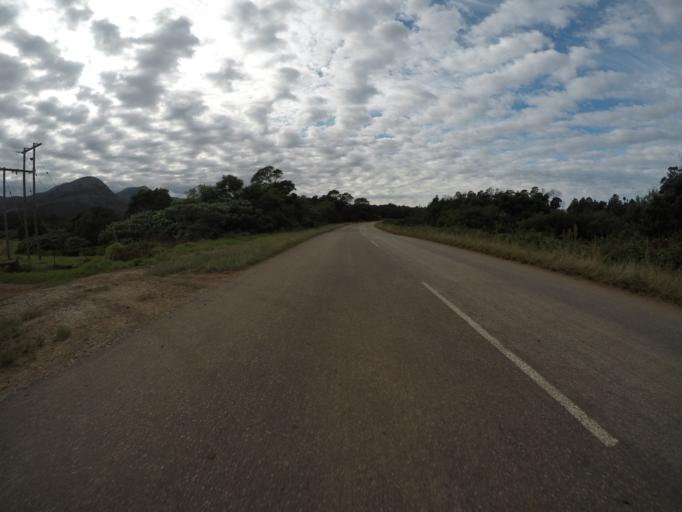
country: ZA
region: Eastern Cape
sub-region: Cacadu District Municipality
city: Kareedouw
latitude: -34.0121
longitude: 24.2953
